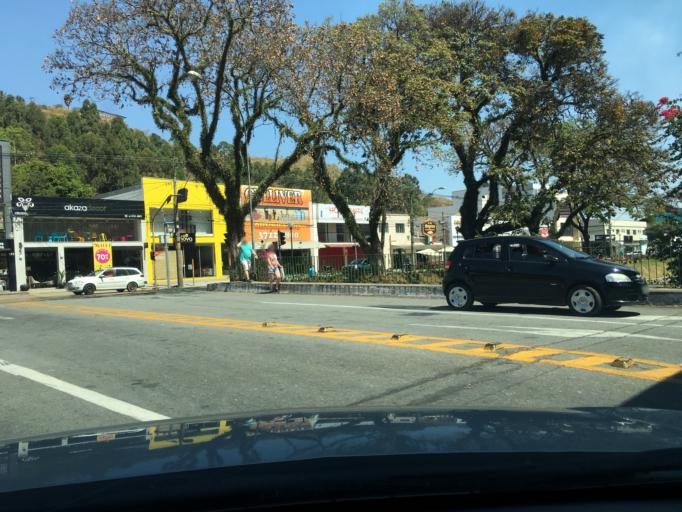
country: BR
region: Minas Gerais
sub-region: Pocos De Caldas
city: Pocos de Caldas
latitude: -21.7858
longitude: -46.5745
